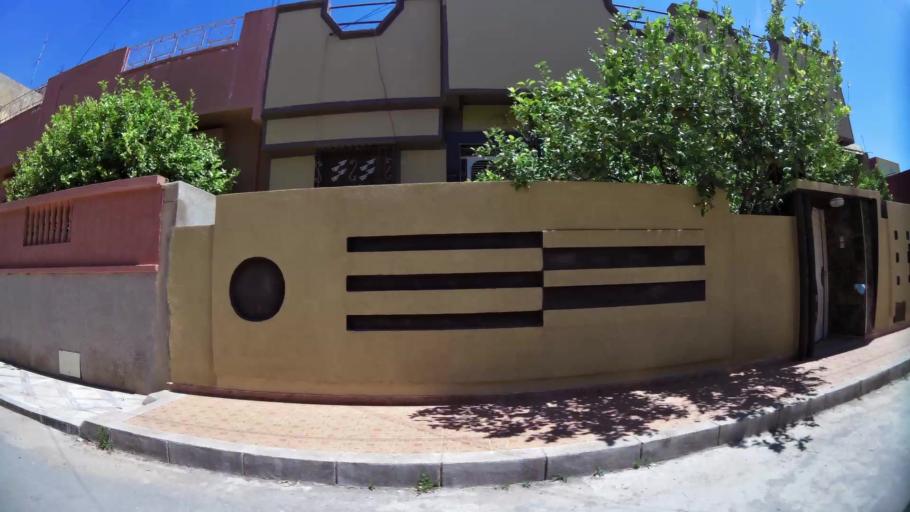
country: MA
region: Oriental
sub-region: Oujda-Angad
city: Oujda
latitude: 34.6630
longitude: -1.9205
